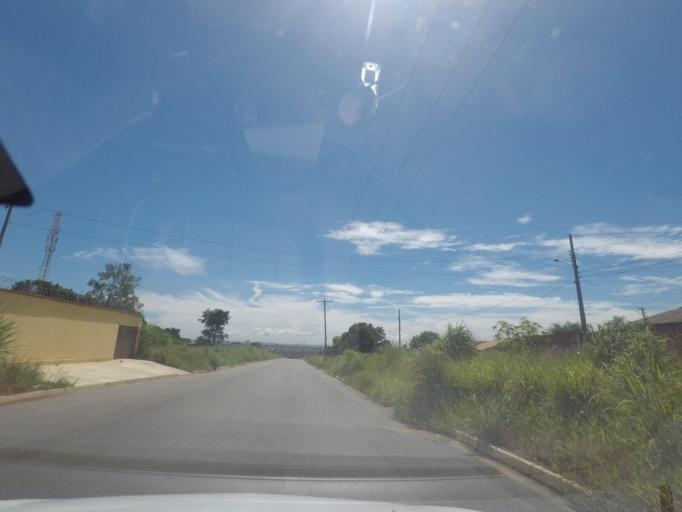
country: BR
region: Goias
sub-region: Aparecida De Goiania
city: Aparecida de Goiania
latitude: -16.7876
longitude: -49.3295
